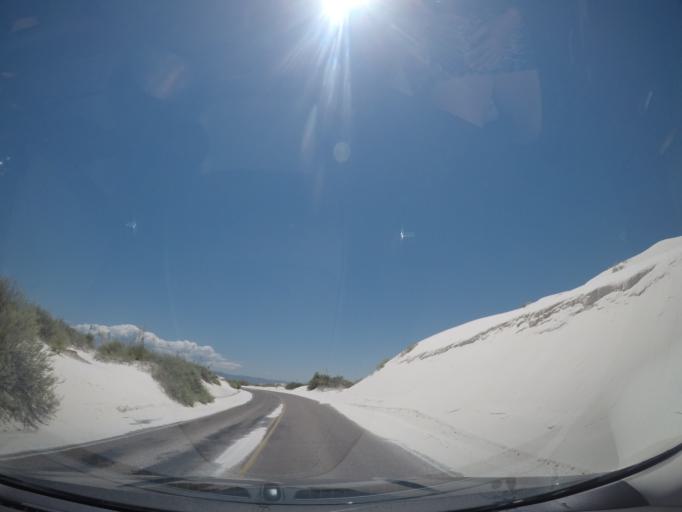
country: US
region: New Mexico
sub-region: Otero County
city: Holloman Air Force Base
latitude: 32.7952
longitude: -106.2159
